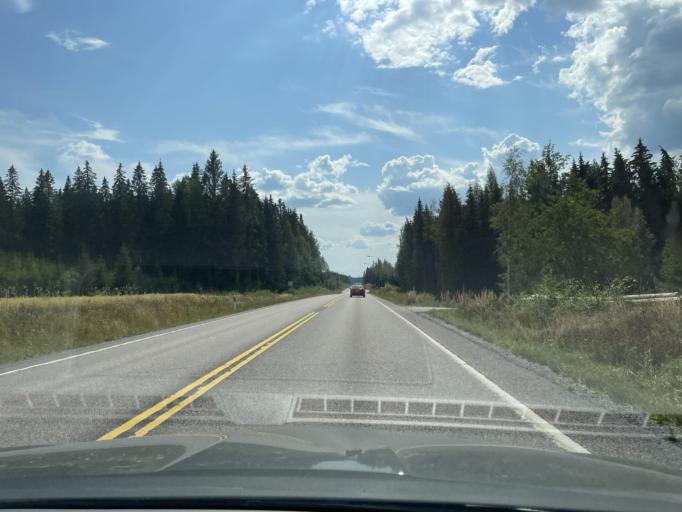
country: FI
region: Central Finland
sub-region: Jaemsae
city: Jaemsae
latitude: 61.9534
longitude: 25.3643
